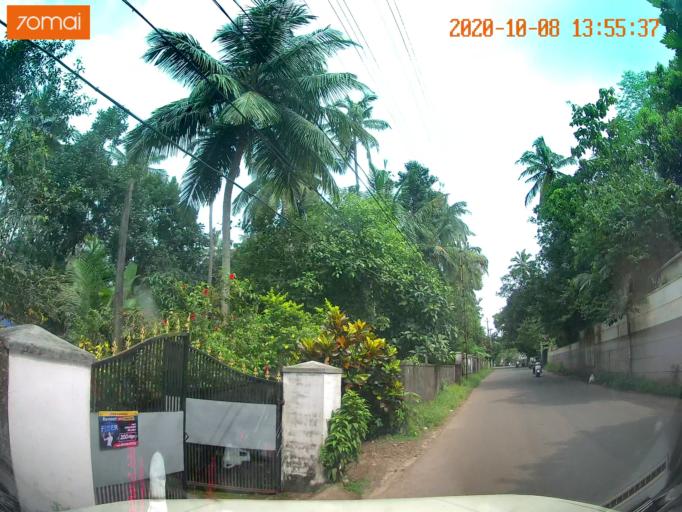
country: IN
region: Kerala
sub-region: Kozhikode
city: Kozhikode
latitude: 11.2933
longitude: 75.7957
